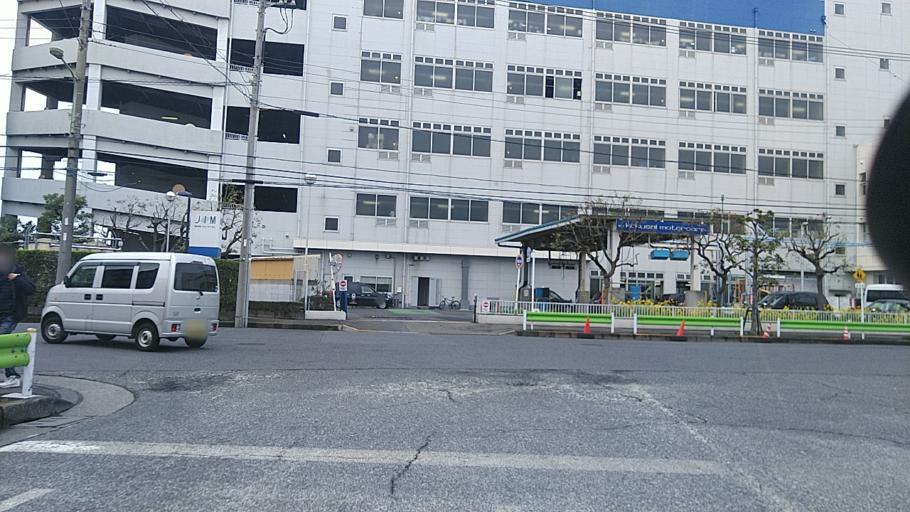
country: JP
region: Kanagawa
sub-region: Kawasaki-shi
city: Kawasaki
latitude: 35.5761
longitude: 139.7455
